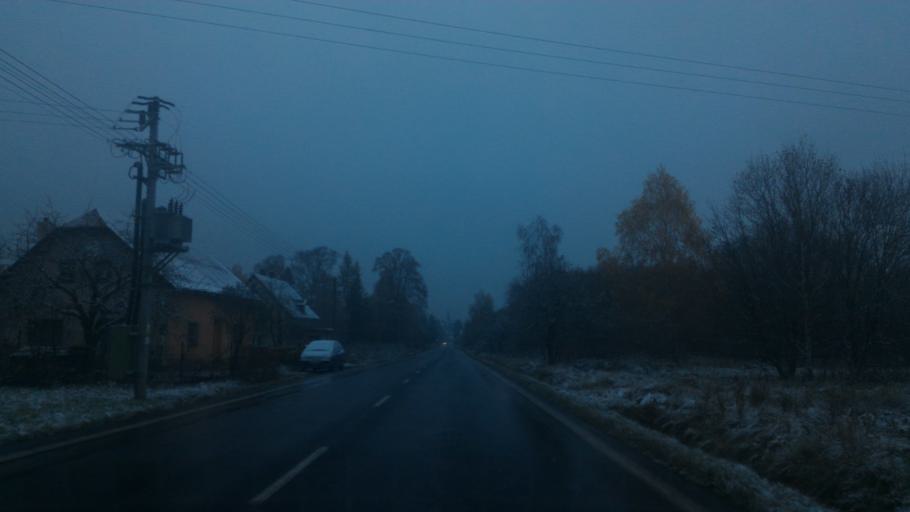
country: CZ
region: Ustecky
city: Jirikov
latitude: 50.9828
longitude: 14.5676
